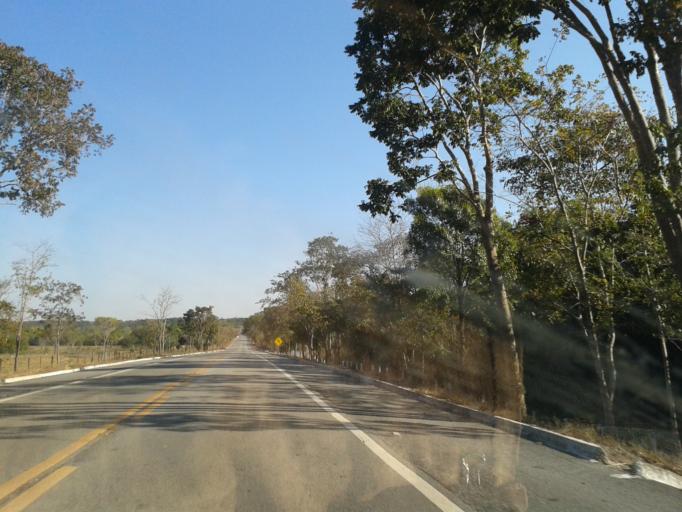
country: BR
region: Goias
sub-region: Mozarlandia
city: Mozarlandia
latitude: -15.1436
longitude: -50.5851
